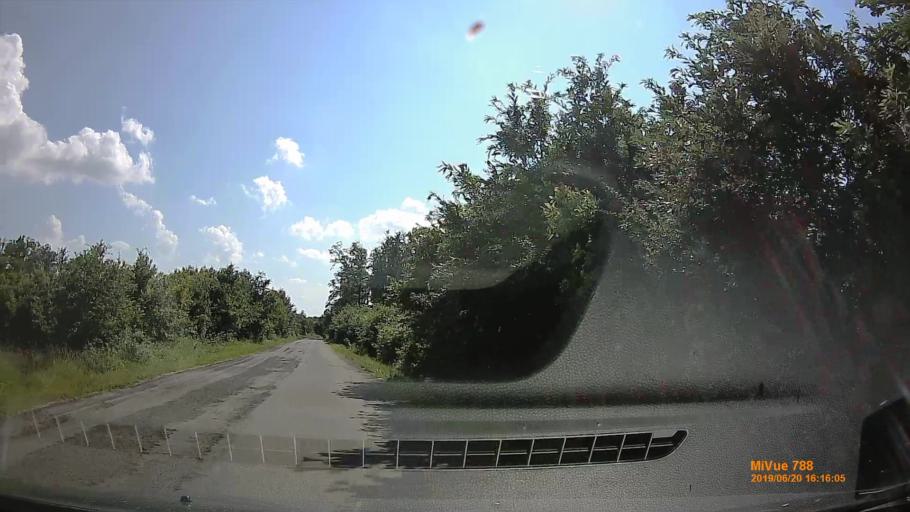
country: HU
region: Baranya
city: Buekkoesd
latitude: 46.0982
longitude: 18.0710
